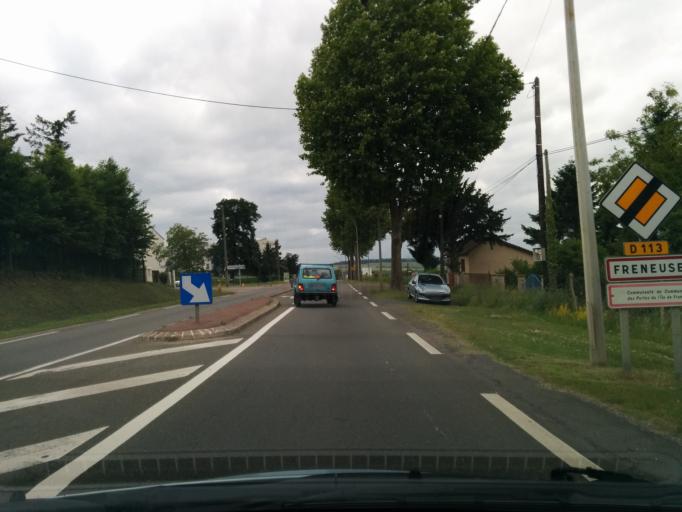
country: FR
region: Ile-de-France
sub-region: Departement des Yvelines
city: Freneuse
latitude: 49.0325
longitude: 1.6031
